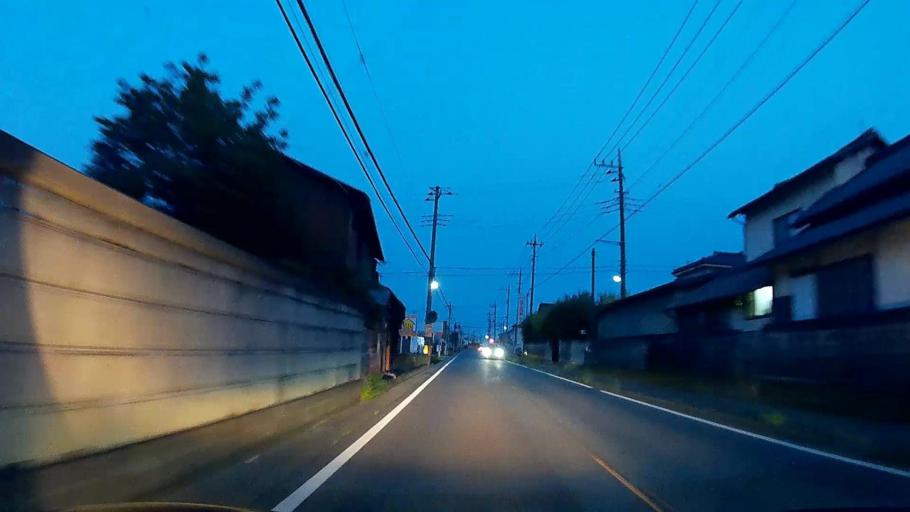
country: JP
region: Gunma
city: Takasaki
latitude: 36.3418
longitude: 138.9703
